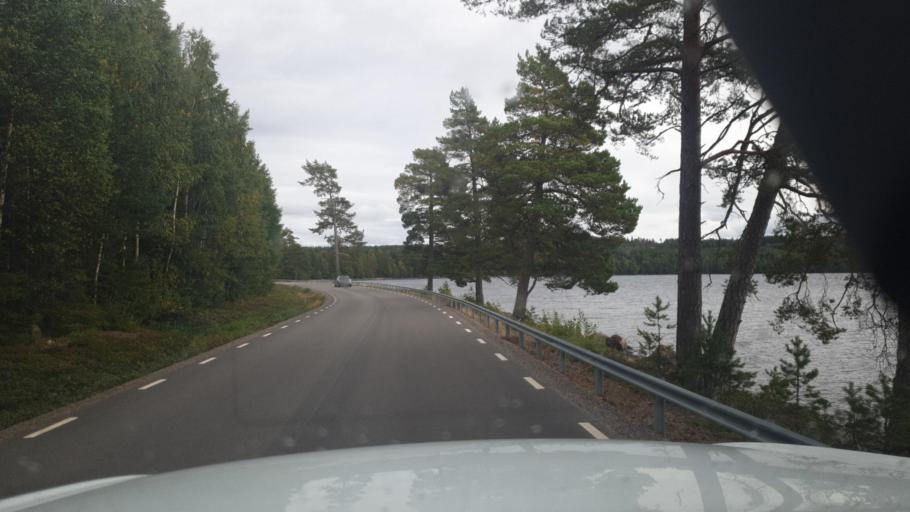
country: SE
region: Vaermland
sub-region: Torsby Kommun
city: Torsby
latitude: 59.9810
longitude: 12.7950
